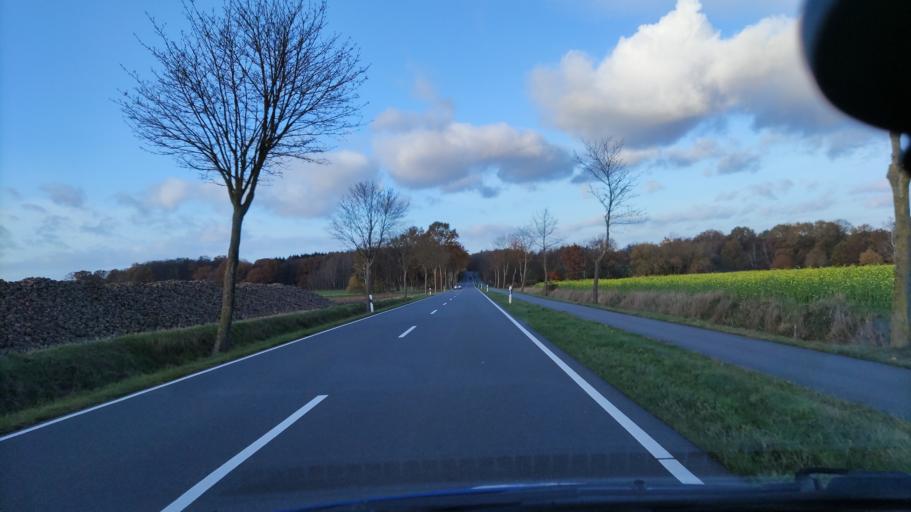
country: DE
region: Lower Saxony
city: Schneverdingen
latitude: 53.0667
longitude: 9.8163
